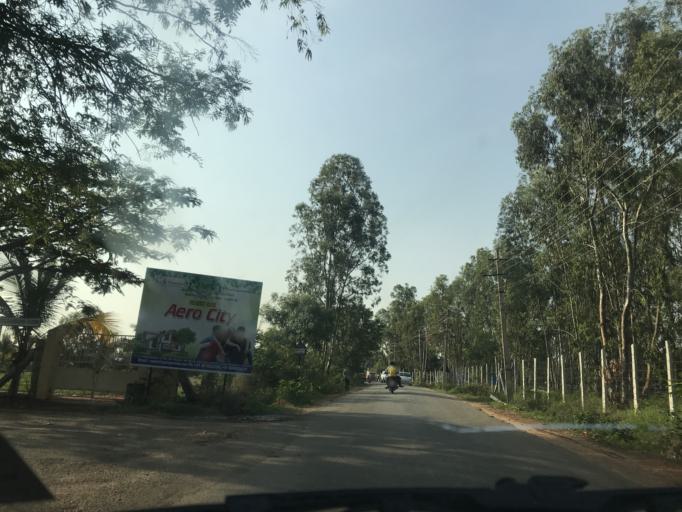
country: IN
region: Karnataka
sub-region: Bangalore Rural
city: Devanhalli
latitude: 13.2002
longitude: 77.6453
